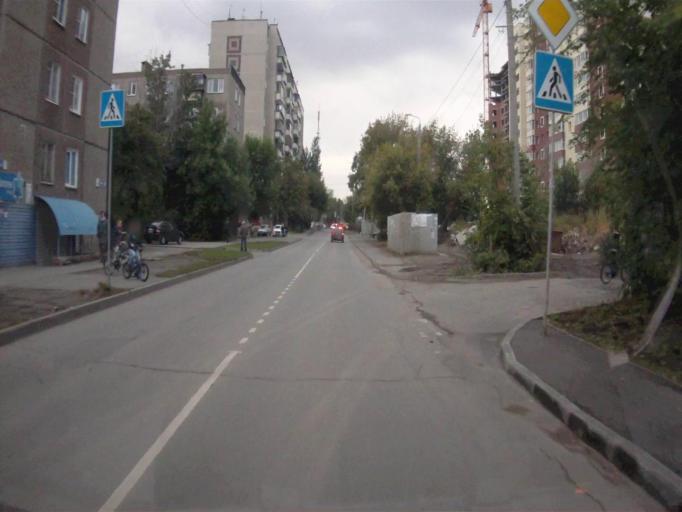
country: RU
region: Chelyabinsk
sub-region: Gorod Chelyabinsk
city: Chelyabinsk
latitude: 55.1442
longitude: 61.3967
